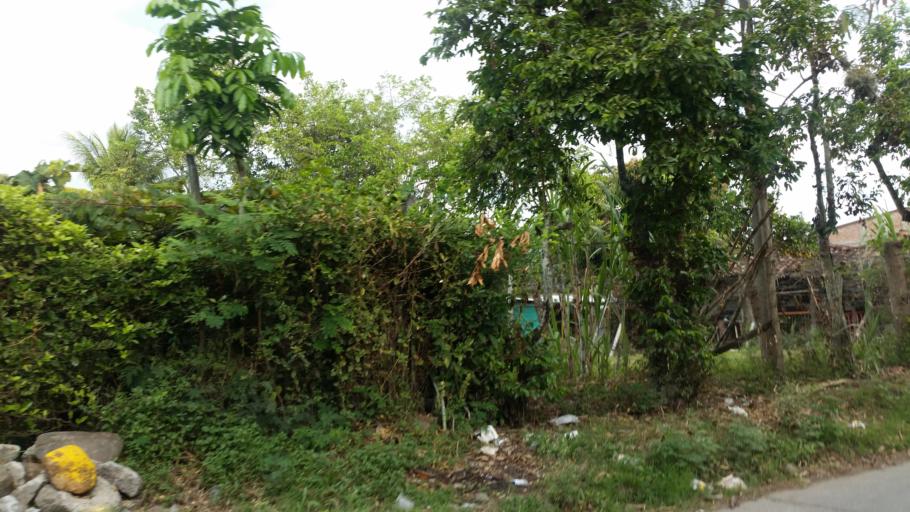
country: CO
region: Valle del Cauca
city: Ginebra
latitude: 3.7296
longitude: -76.2621
